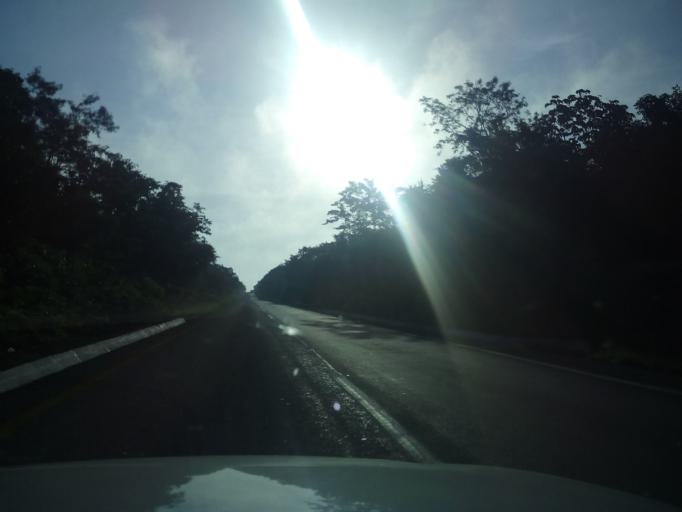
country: MX
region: Yucatan
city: Piste
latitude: 20.7479
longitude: -88.7082
